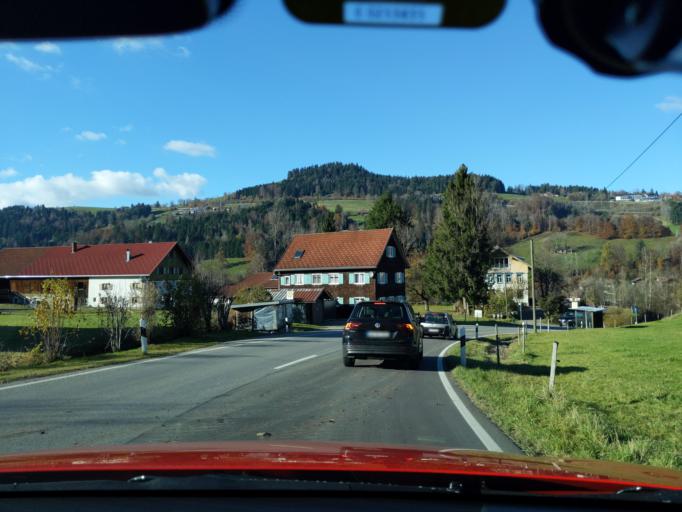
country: DE
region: Bavaria
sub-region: Swabia
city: Oberstaufen
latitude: 47.5390
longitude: 10.0175
